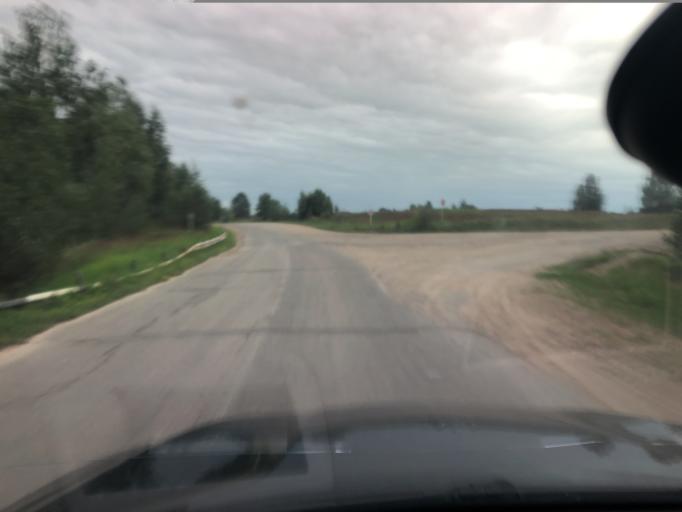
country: RU
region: Jaroslavl
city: Petrovsk
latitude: 56.9845
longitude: 39.1391
